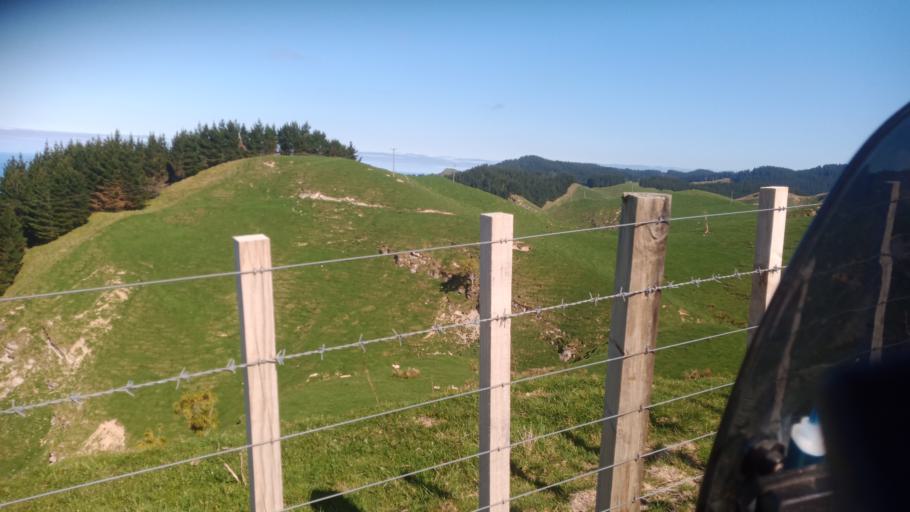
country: NZ
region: Gisborne
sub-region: Gisborne District
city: Gisborne
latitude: -39.1611
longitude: 177.9048
